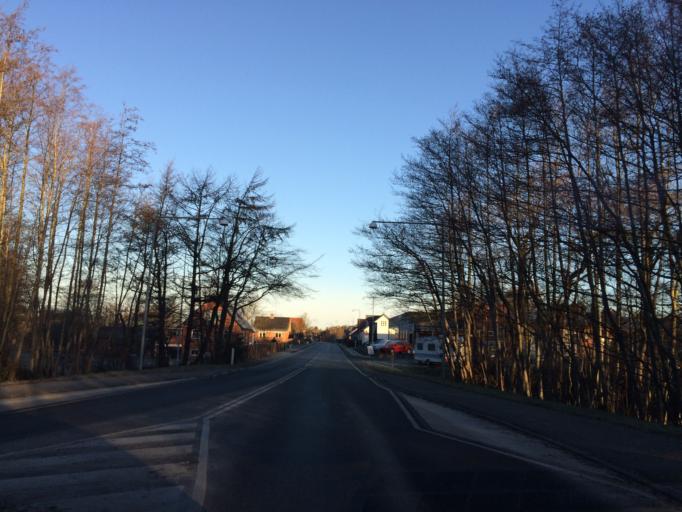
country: DK
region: Central Jutland
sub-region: Holstebro Kommune
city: Ulfborg
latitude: 56.4071
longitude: 8.3135
